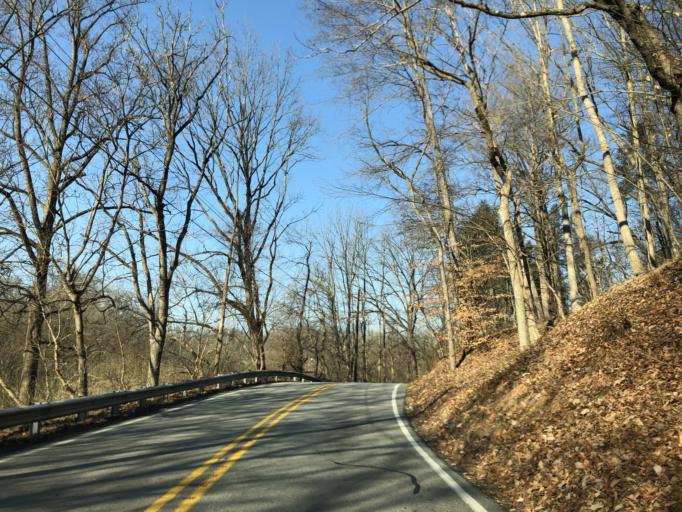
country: US
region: Pennsylvania
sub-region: Chester County
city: Chesterbrook
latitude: 40.0967
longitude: -75.4615
